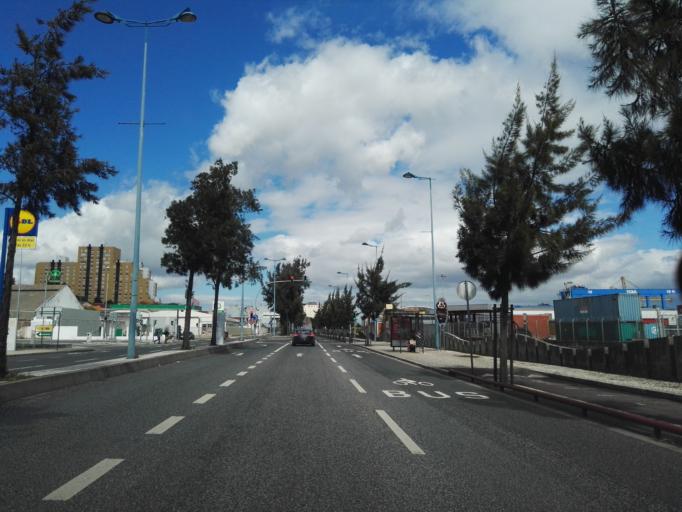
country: PT
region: Lisbon
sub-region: Lisbon
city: Lisbon
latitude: 38.7244
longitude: -9.1120
